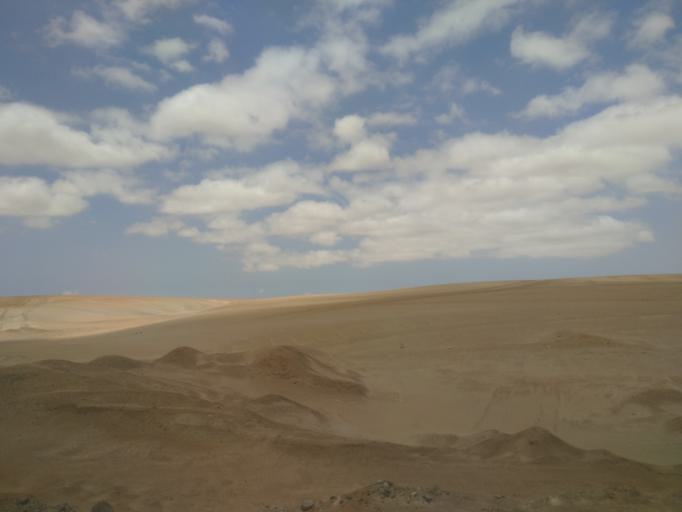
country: PE
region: Arequipa
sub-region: Provincia de Islay
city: Cocachacra
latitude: -17.1070
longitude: -71.5254
